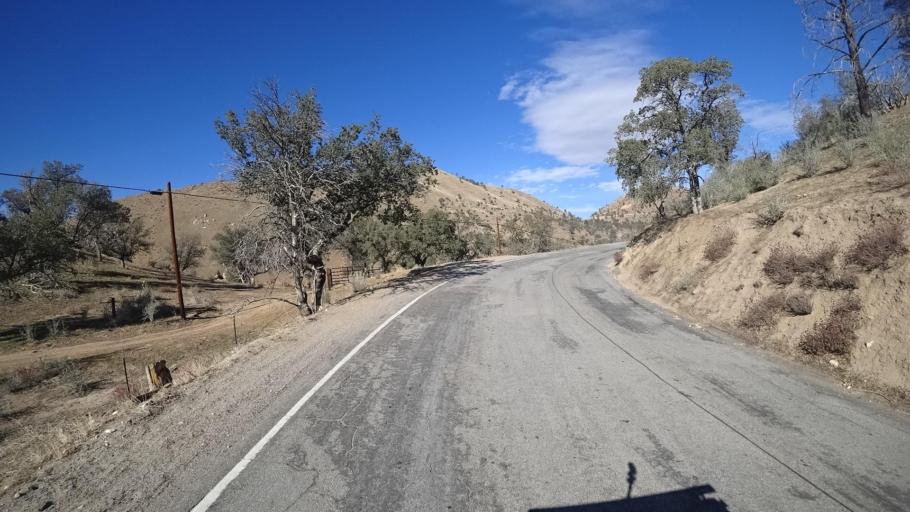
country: US
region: California
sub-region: Kern County
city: Bodfish
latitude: 35.5586
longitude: -118.5108
